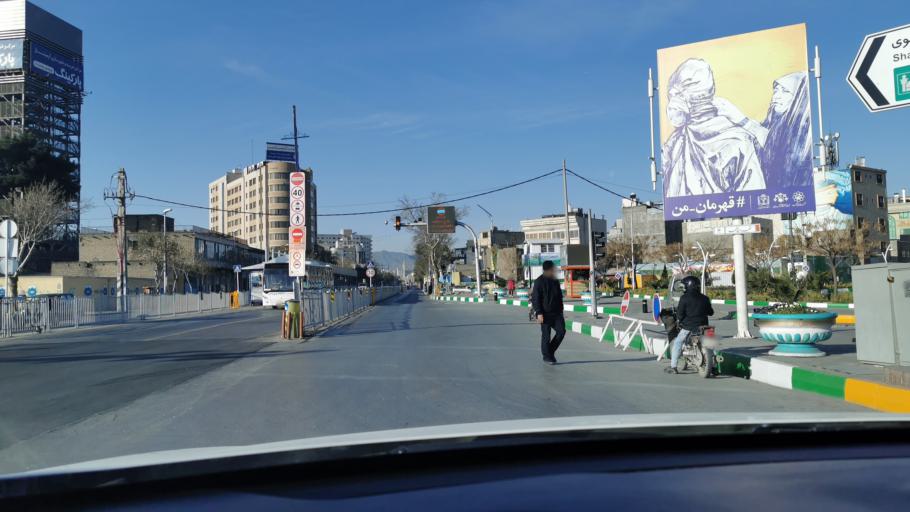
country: IR
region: Razavi Khorasan
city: Mashhad
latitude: 36.2959
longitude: 59.6281
